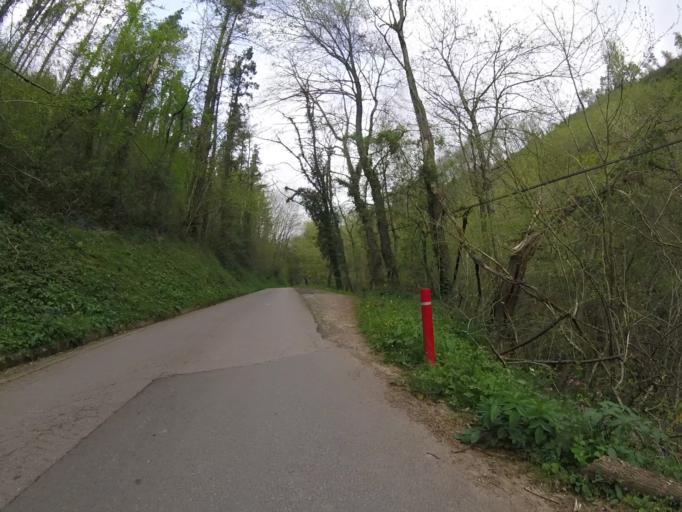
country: ES
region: Basque Country
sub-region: Provincia de Guipuzcoa
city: Anoeta
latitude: 43.1679
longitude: -2.0792
